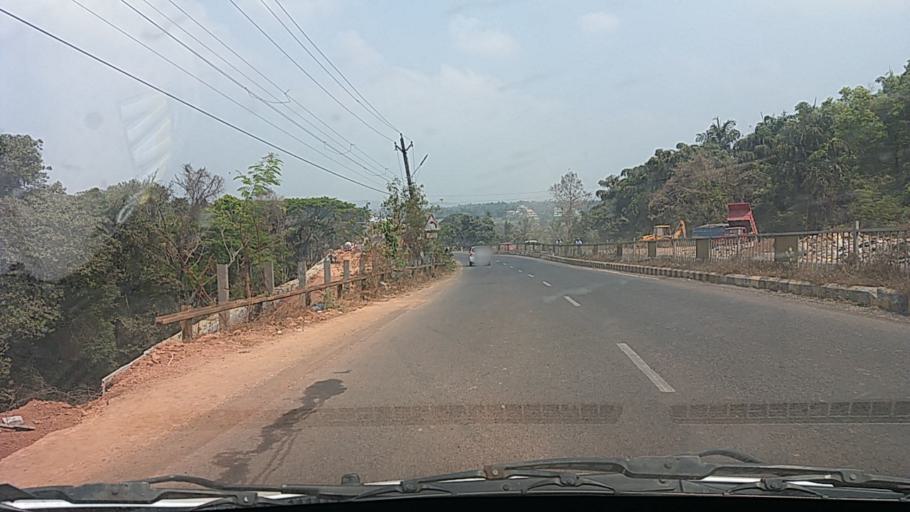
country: IN
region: Goa
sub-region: North Goa
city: Bambolim
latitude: 15.4679
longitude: 73.8510
